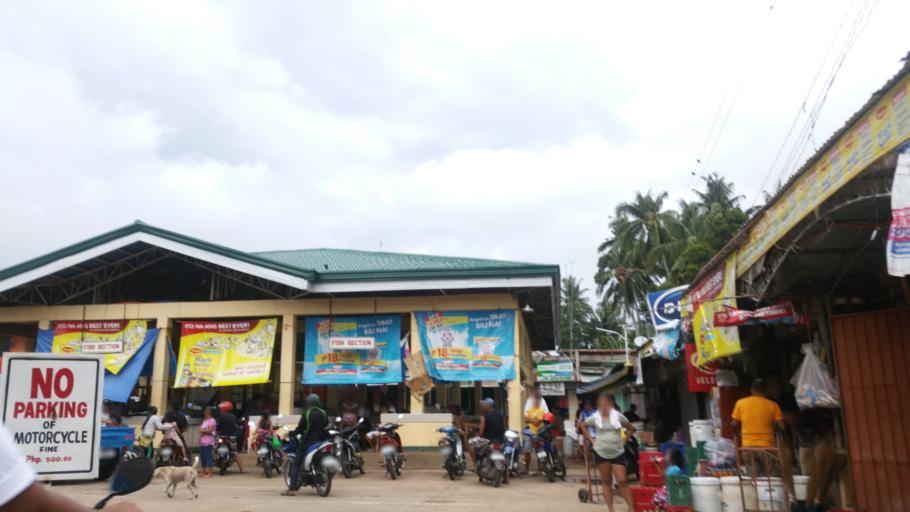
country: PH
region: Central Visayas
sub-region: Province of Siquijor
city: Lazi
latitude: 9.1260
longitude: 123.6359
